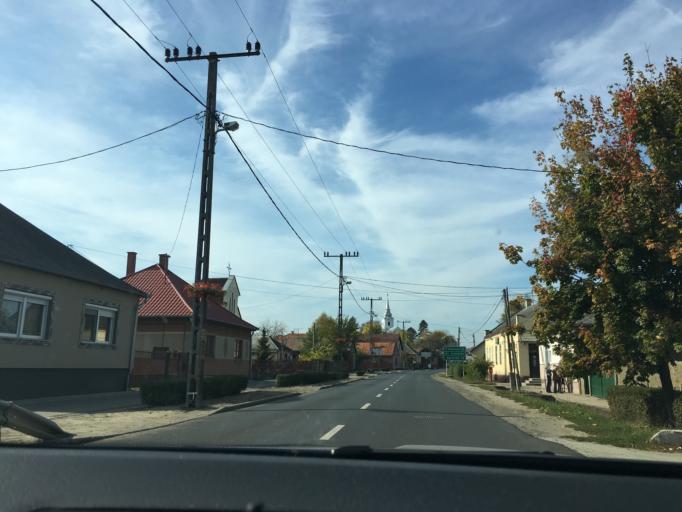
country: HU
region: Hajdu-Bihar
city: Vamospercs
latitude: 47.5248
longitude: 21.9027
